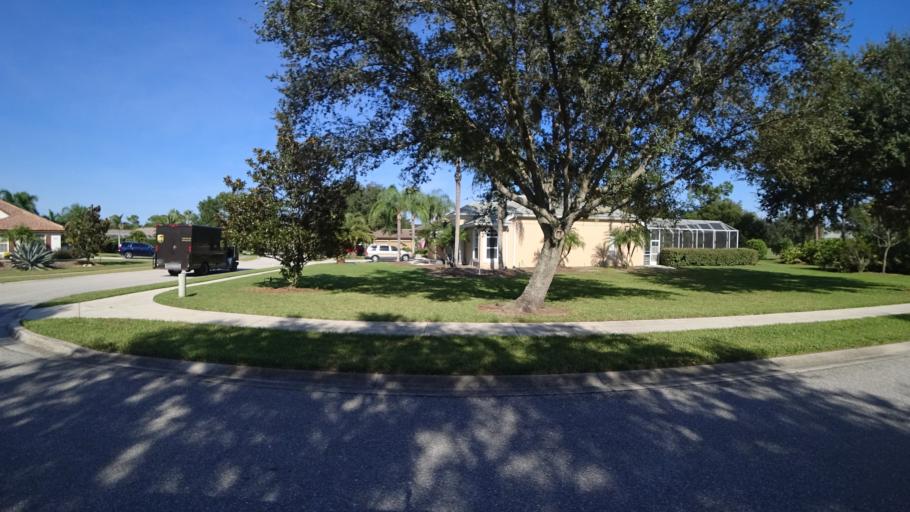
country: US
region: Florida
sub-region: Sarasota County
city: The Meadows
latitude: 27.4161
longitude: -82.4389
